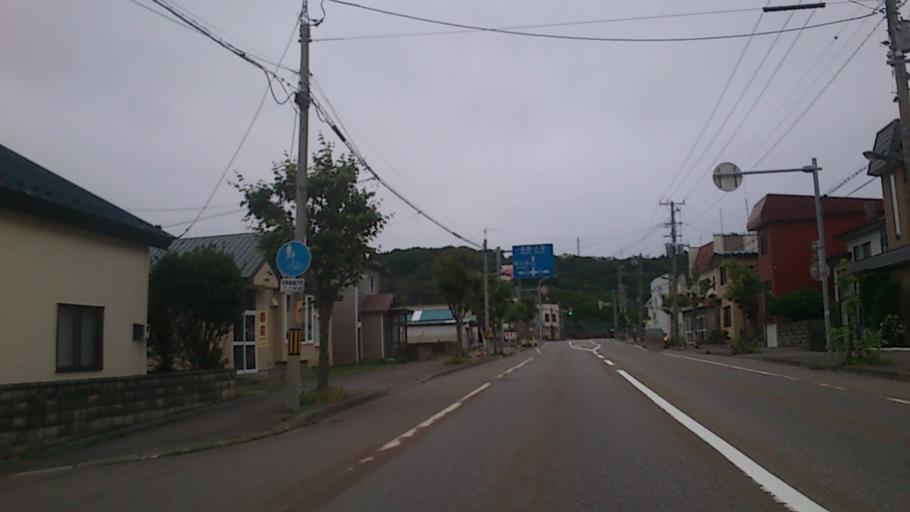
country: JP
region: Hokkaido
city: Kamiiso
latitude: 41.9713
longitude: 140.1387
